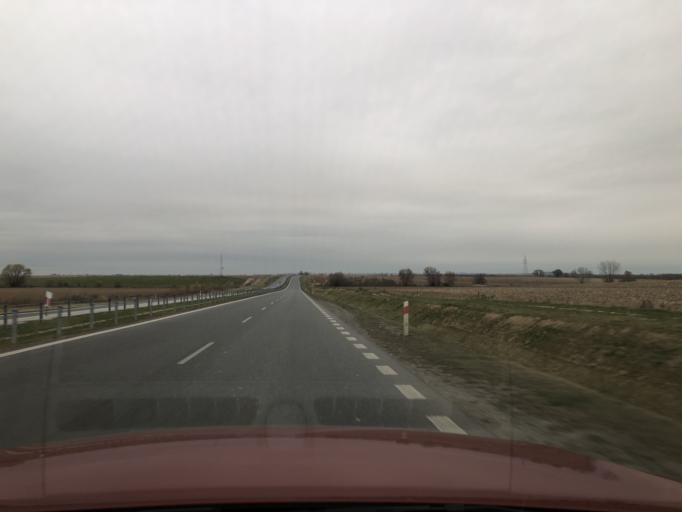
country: PL
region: Lower Silesian Voivodeship
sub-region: Powiat swidnicki
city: Swidnica
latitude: 50.8433
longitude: 16.4348
